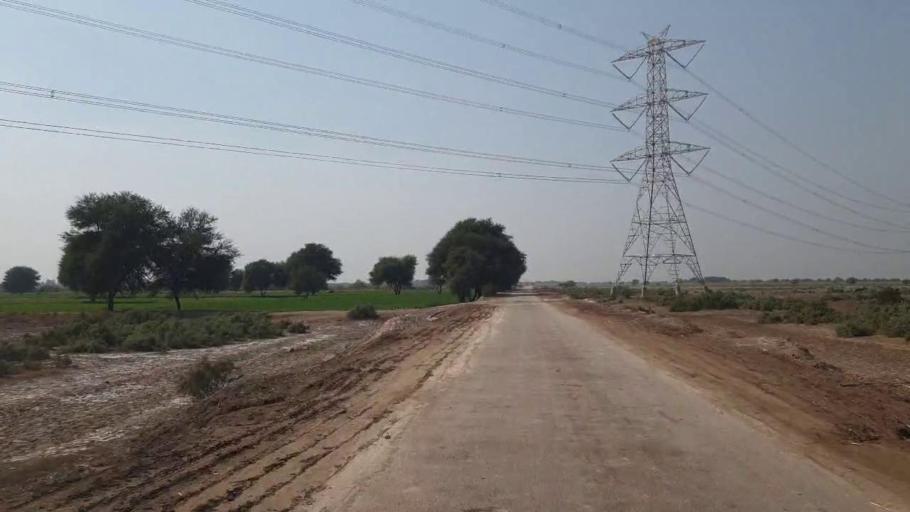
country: PK
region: Sindh
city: Chambar
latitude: 25.3811
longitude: 68.8904
